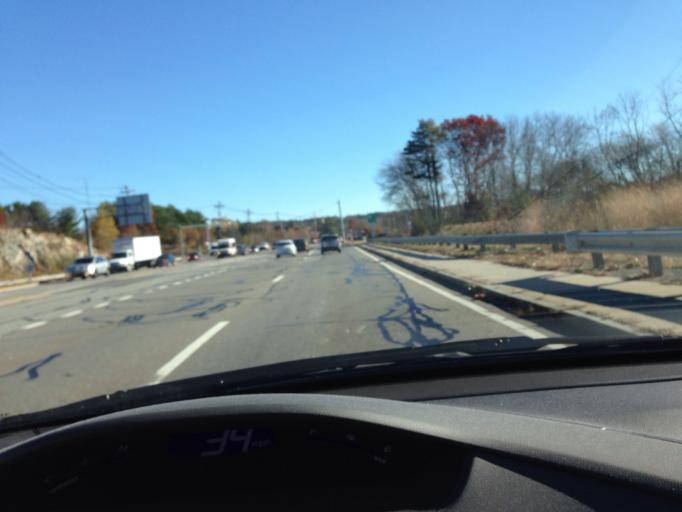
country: US
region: Massachusetts
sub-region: Middlesex County
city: Pinehurst
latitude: 42.5021
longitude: -71.2426
